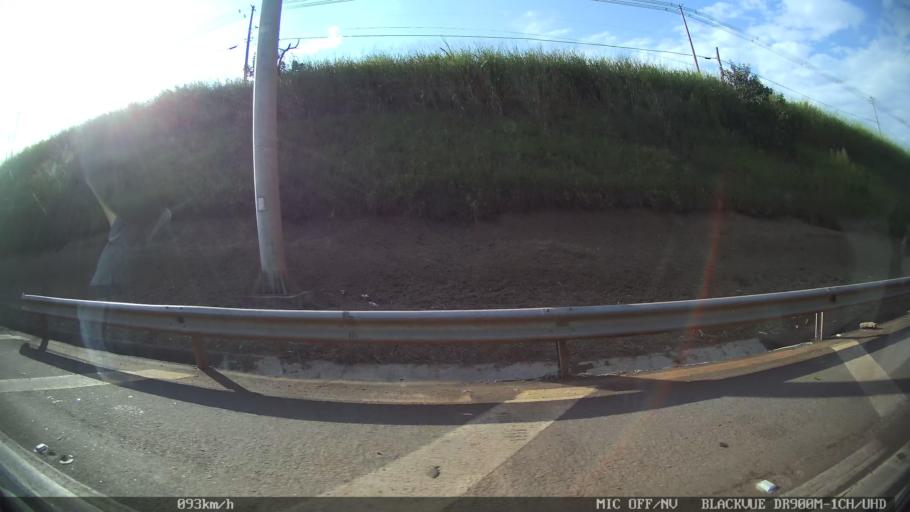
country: BR
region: Sao Paulo
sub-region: Cosmopolis
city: Cosmopolis
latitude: -22.6564
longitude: -47.1767
